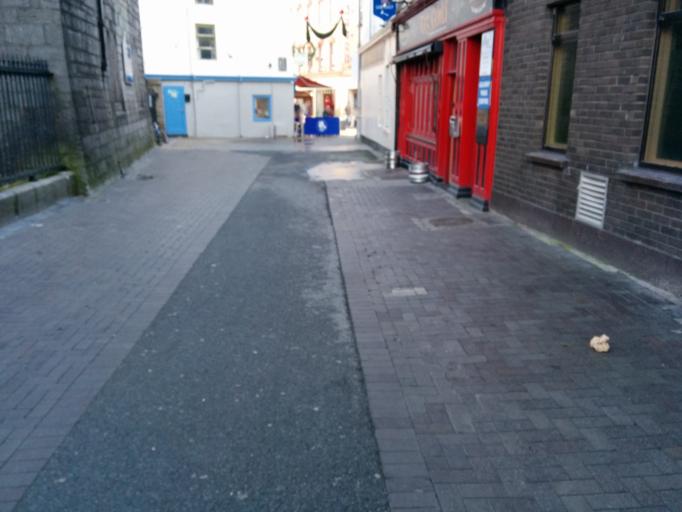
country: IE
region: Connaught
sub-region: County Galway
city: Gaillimh
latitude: 53.2726
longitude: -9.0538
